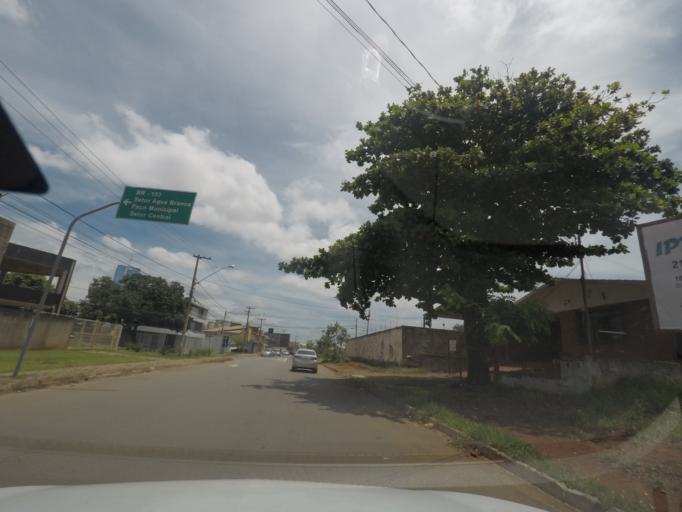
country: BR
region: Goias
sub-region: Goiania
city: Goiania
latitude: -16.6910
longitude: -49.2337
